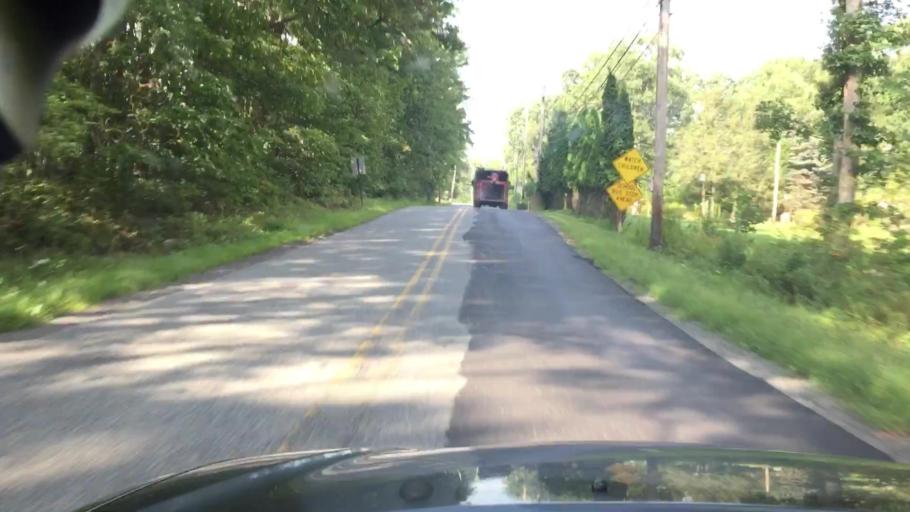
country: US
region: Pennsylvania
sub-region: Luzerne County
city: Harleigh
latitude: 41.0589
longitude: -75.9663
